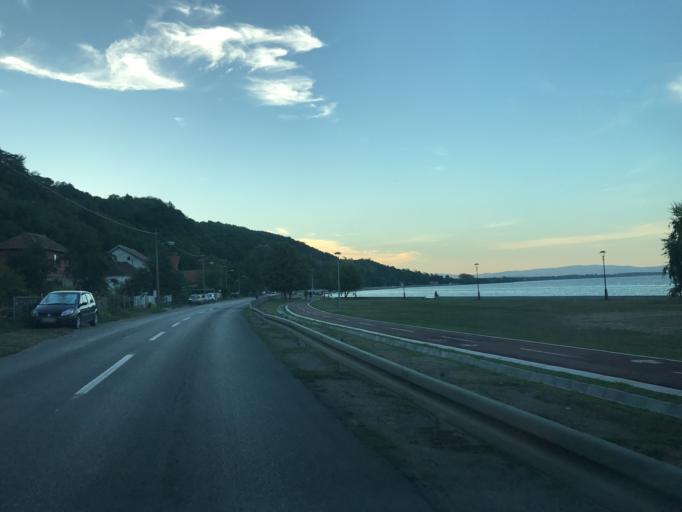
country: RS
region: Central Serbia
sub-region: Branicevski Okrug
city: Golubac
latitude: 44.6550
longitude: 21.6219
